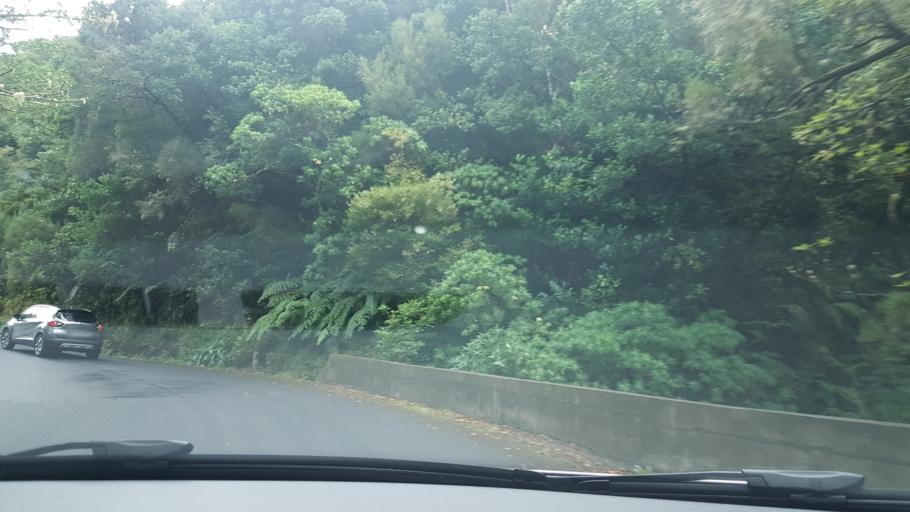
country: PT
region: Madeira
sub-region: Sao Vicente
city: Sao Vicente
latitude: 32.7616
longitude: -17.0205
